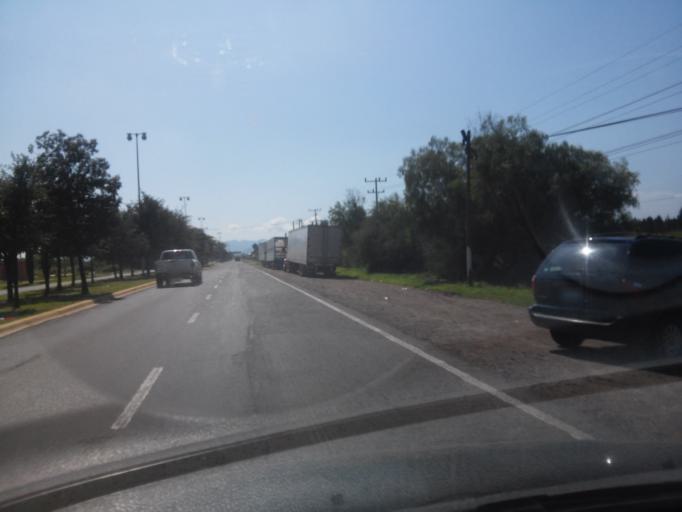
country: MX
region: Durango
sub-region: Durango
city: Sebastian Lerdo de Tejada
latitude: 23.9920
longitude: -104.6261
